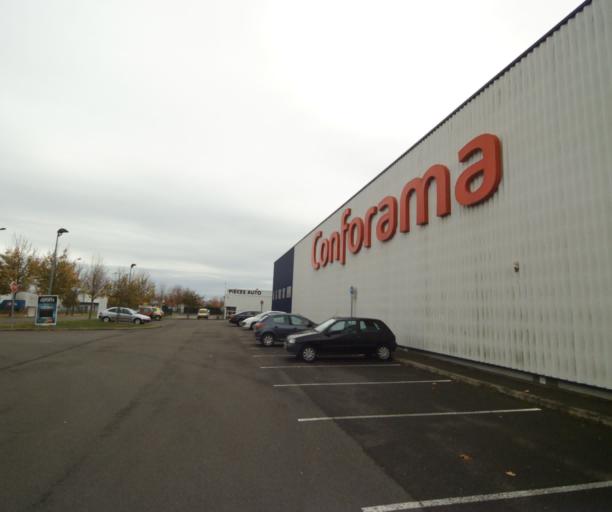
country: FR
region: Centre
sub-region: Departement d'Eure-et-Loir
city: Dreux
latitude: 48.7501
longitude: 1.3516
